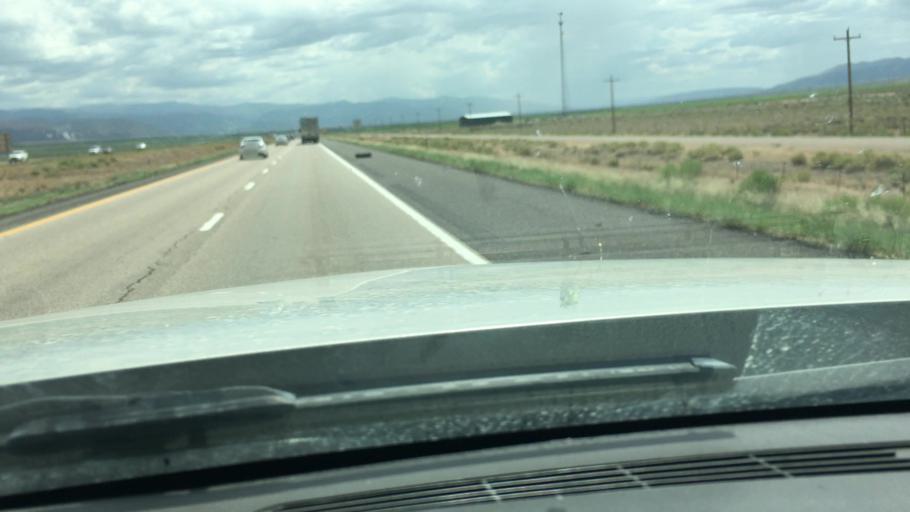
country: US
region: Utah
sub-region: Beaver County
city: Beaver
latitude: 38.0562
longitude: -112.6972
